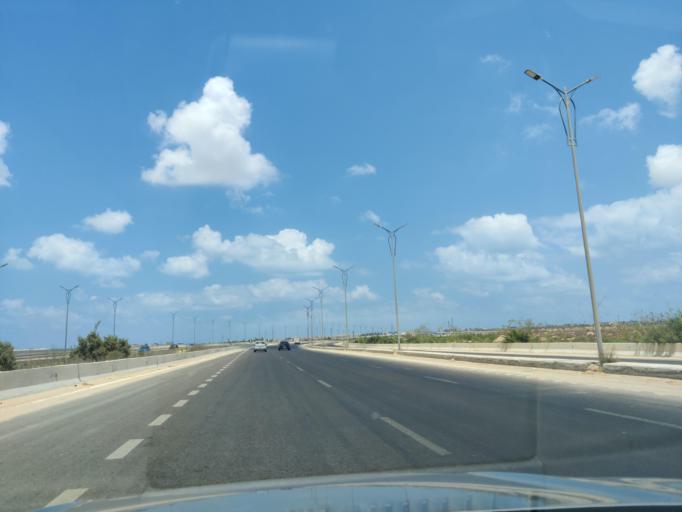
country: EG
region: Alexandria
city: Alexandria
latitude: 30.9896
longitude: 29.6524
